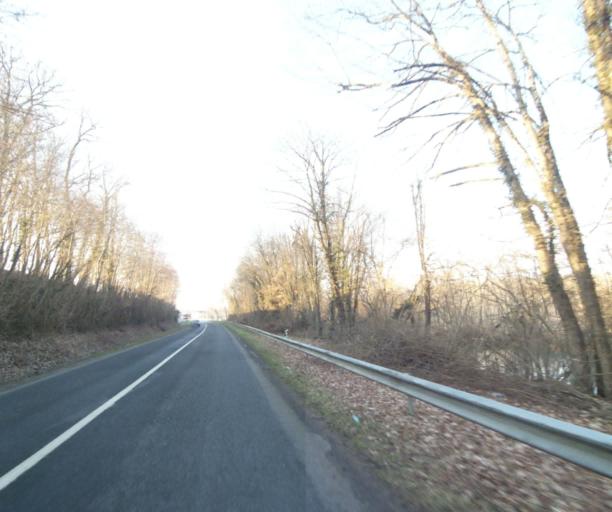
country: FR
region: Champagne-Ardenne
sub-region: Departement de la Haute-Marne
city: Bienville
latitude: 48.5598
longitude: 5.0566
